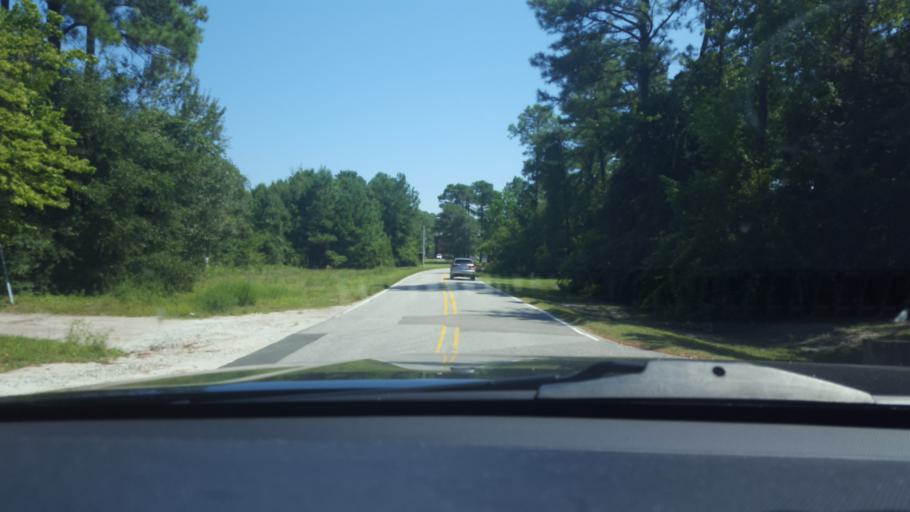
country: US
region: North Carolina
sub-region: New Hanover County
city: Ogden
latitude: 34.2556
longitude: -77.8295
